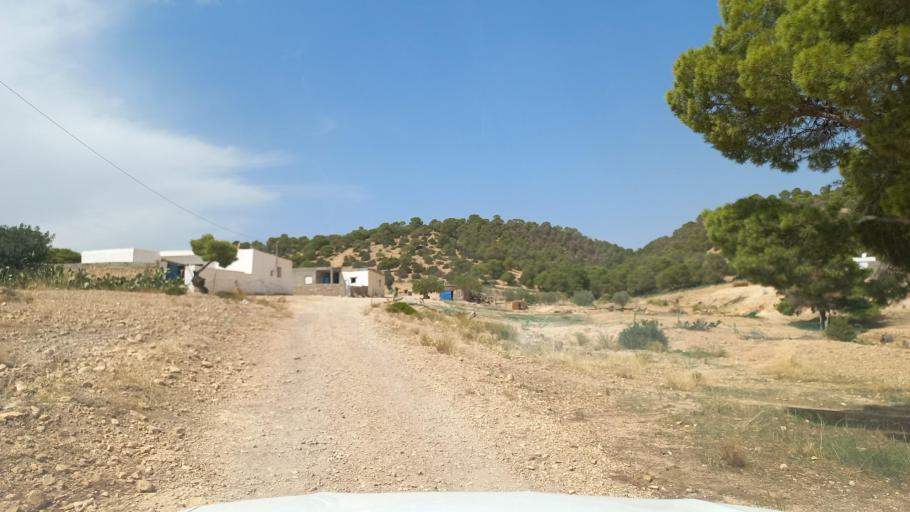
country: TN
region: Al Qasrayn
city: Kasserine
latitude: 35.3743
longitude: 8.8957
